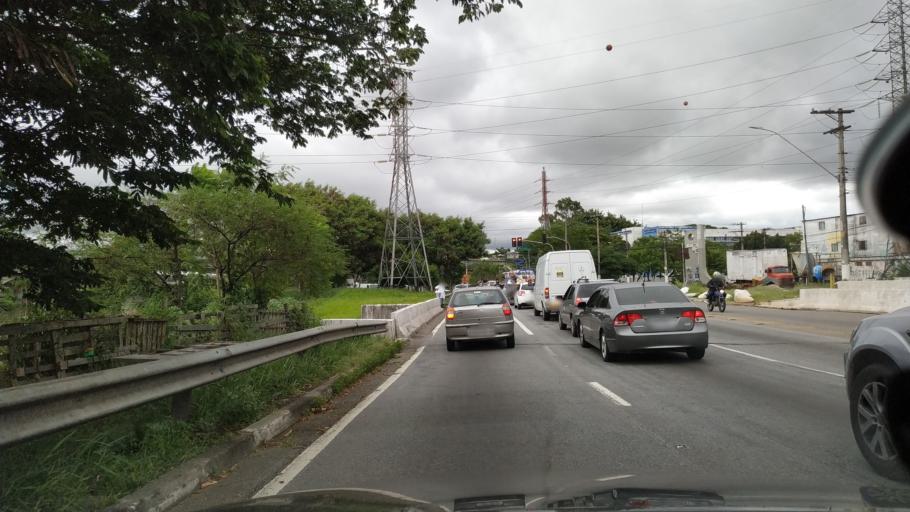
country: BR
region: Sao Paulo
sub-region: Osasco
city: Osasco
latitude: -23.5209
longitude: -46.7863
